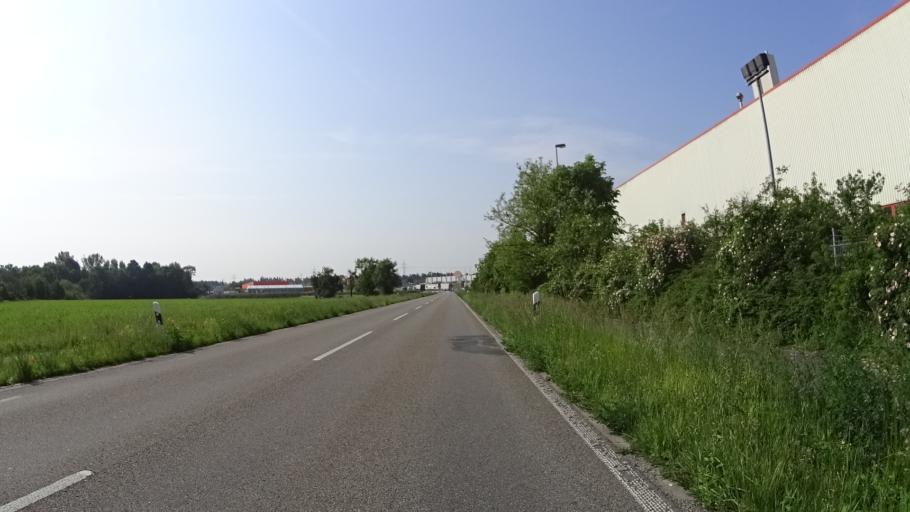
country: DE
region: Baden-Wuerttemberg
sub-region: Karlsruhe Region
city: Hambrucken
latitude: 49.2164
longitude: 8.5272
